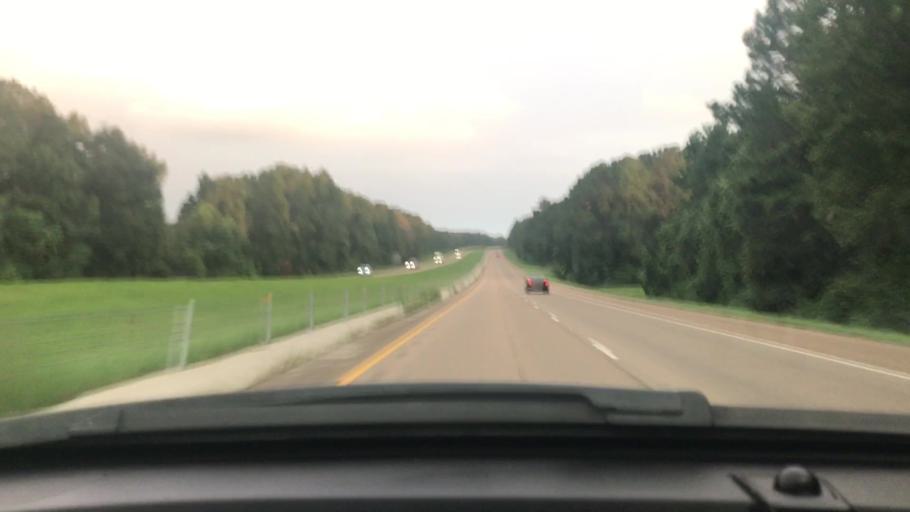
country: US
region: Louisiana
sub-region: Tangipahoa Parish
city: Kentwood
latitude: 30.9229
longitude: -90.5245
